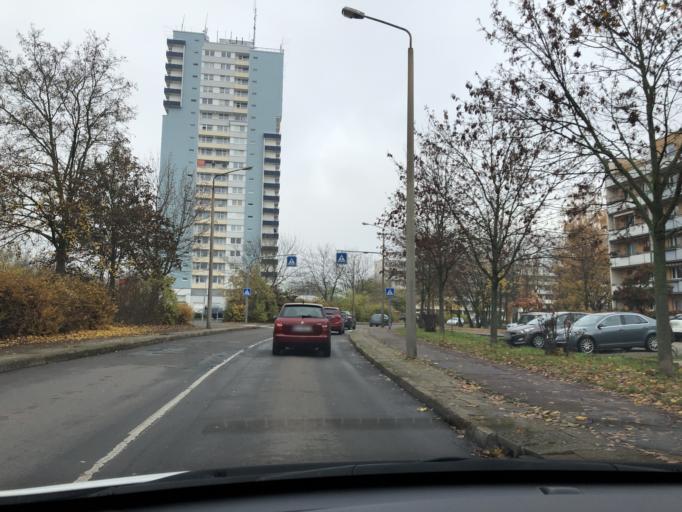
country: DE
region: Saxony-Anhalt
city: Halle Neustadt
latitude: 51.4828
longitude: 11.9349
